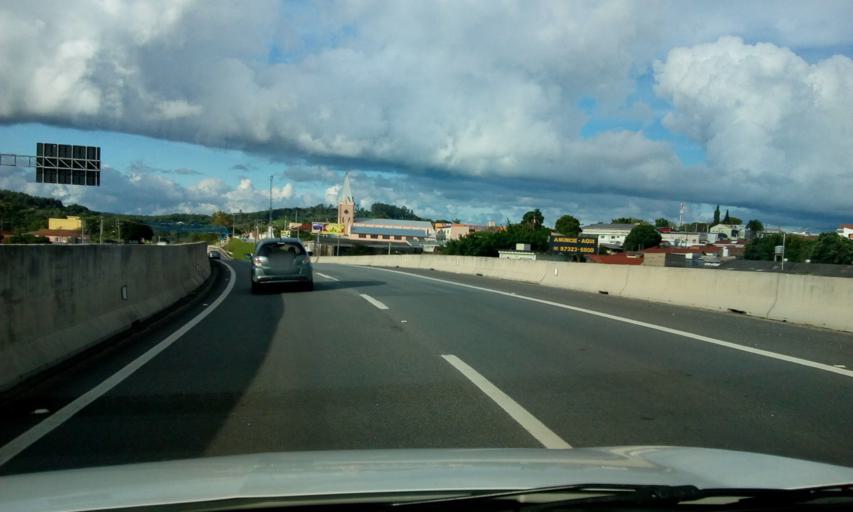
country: BR
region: Sao Paulo
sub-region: Jundiai
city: Jundiai
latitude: -23.1531
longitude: -46.8783
